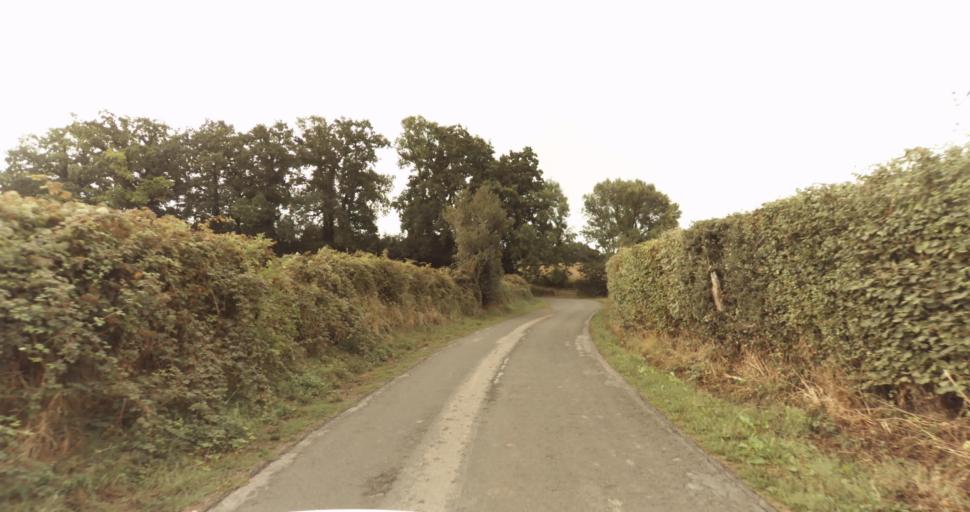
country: FR
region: Lower Normandy
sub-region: Departement de l'Orne
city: Trun
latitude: 48.9103
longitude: 0.1007
